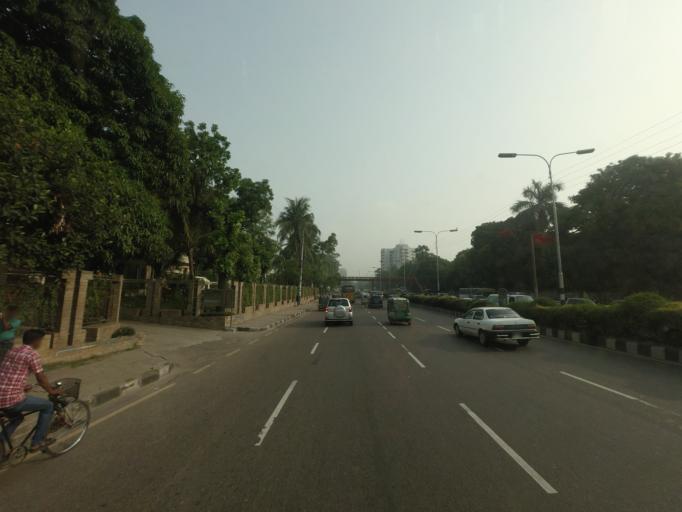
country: BD
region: Dhaka
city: Azimpur
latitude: 23.7696
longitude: 90.3893
